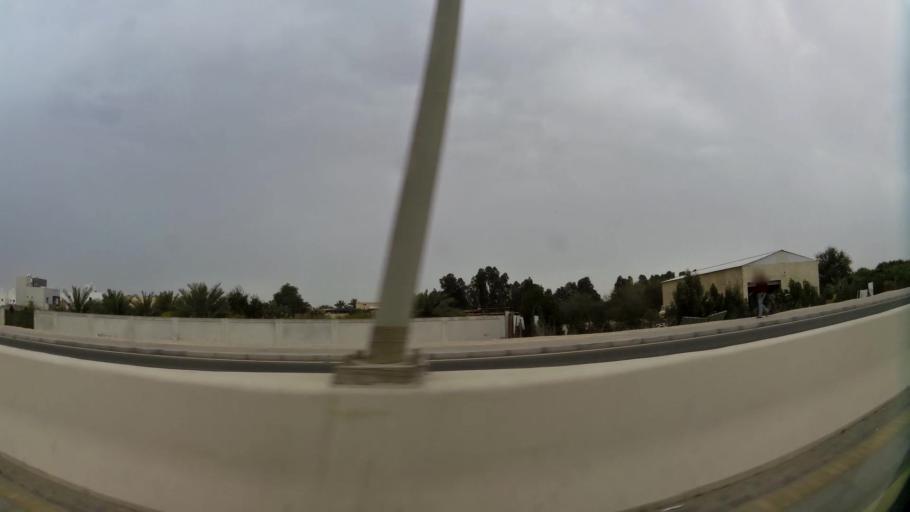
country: BH
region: Central Governorate
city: Dar Kulayb
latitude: 26.0830
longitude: 50.4977
